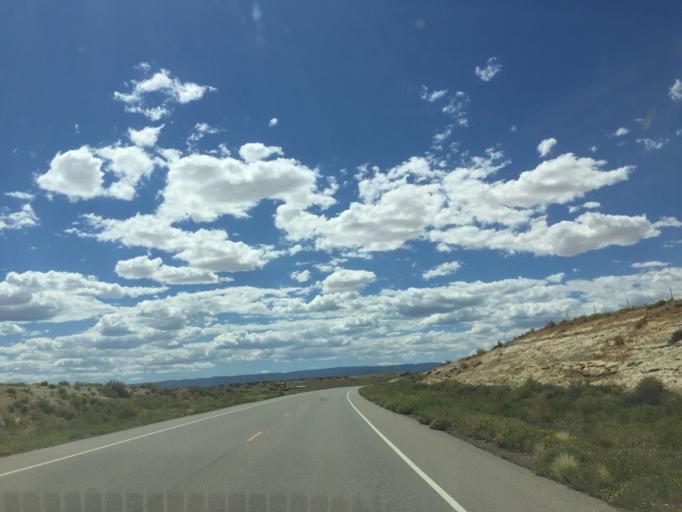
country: US
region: New Mexico
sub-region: San Juan County
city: Shiprock
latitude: 36.3471
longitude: -108.6434
